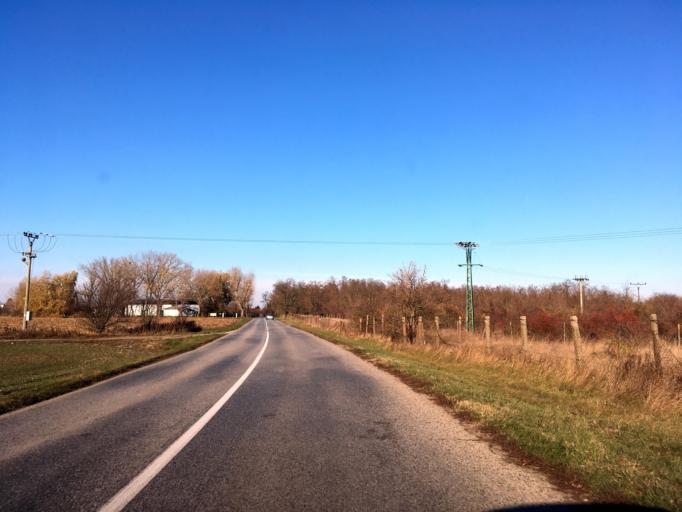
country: SK
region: Nitriansky
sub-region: Okres Komarno
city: Hurbanovo
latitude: 47.9144
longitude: 18.1369
